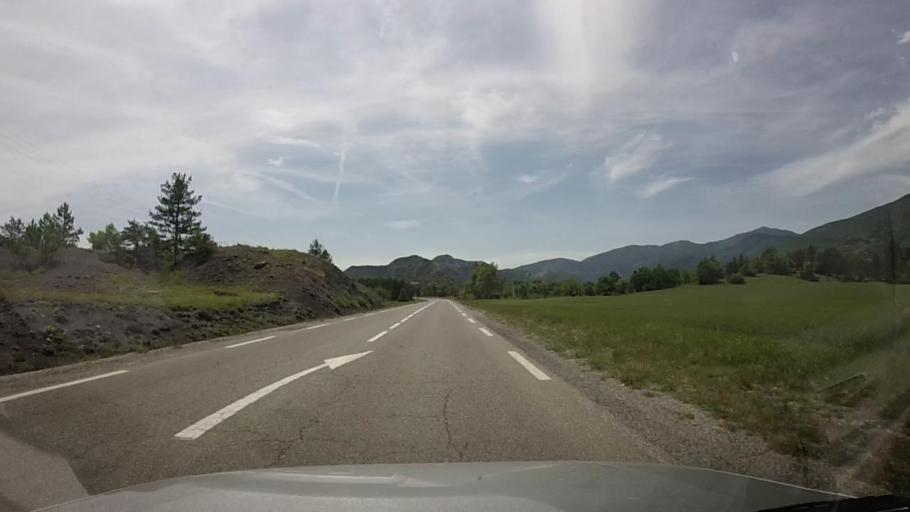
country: FR
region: Provence-Alpes-Cote d'Azur
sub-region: Departement des Alpes-de-Haute-Provence
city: Le Brusquet
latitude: 44.1391
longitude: 6.2912
